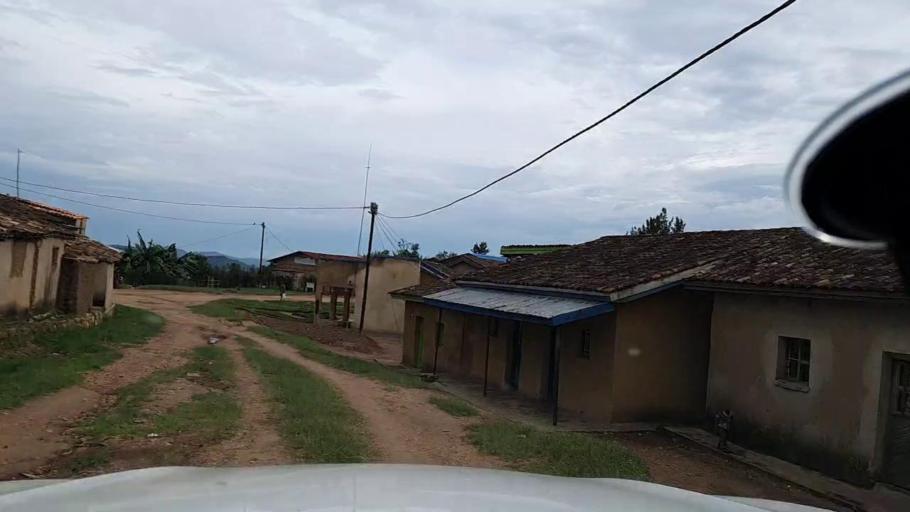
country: RW
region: Southern Province
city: Gitarama
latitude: -2.1291
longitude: 29.6564
